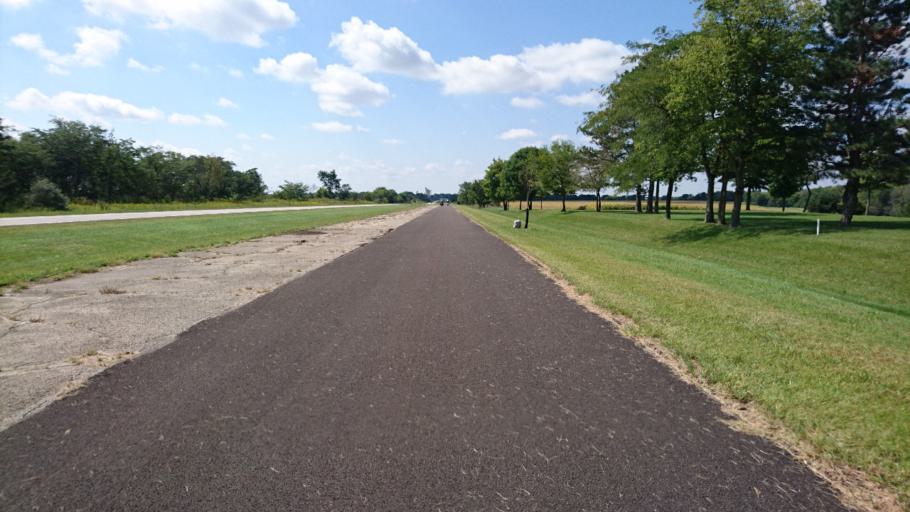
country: US
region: Illinois
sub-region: McLean County
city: Lexington
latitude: 40.5789
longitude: -88.8764
